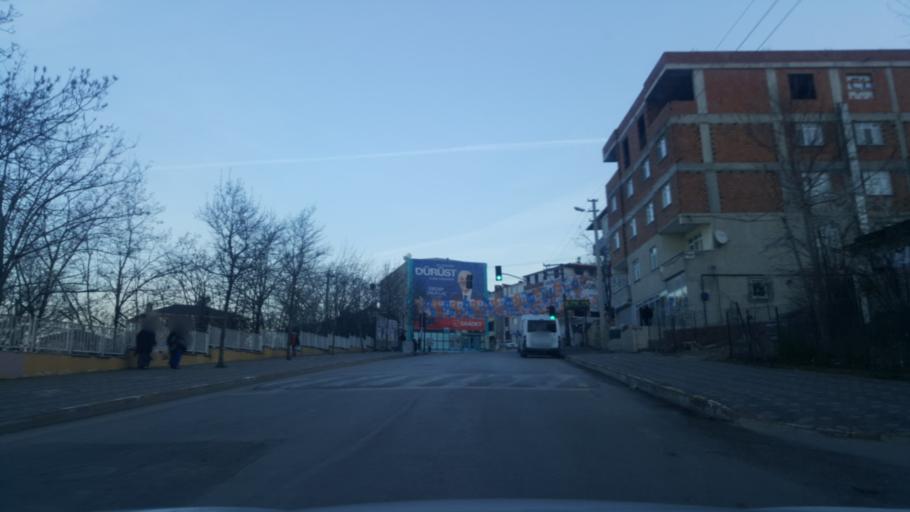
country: TR
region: Kocaeli
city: Tavsancil
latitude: 40.7885
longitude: 29.5387
